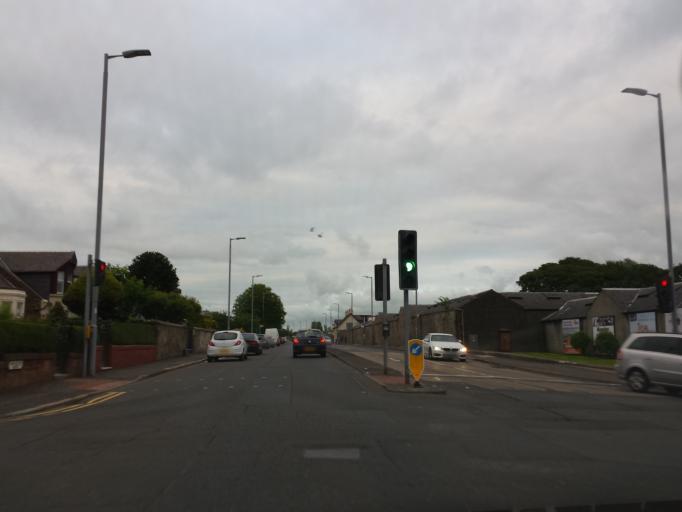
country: GB
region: Scotland
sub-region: South Ayrshire
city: Prestwick
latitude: 55.4674
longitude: -4.6180
